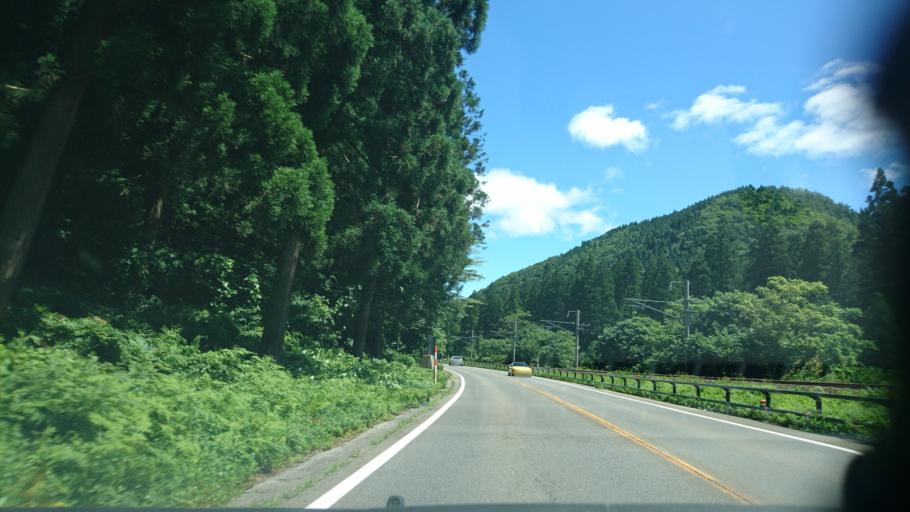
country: JP
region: Akita
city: Kakunodatemachi
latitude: 39.6446
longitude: 140.6634
